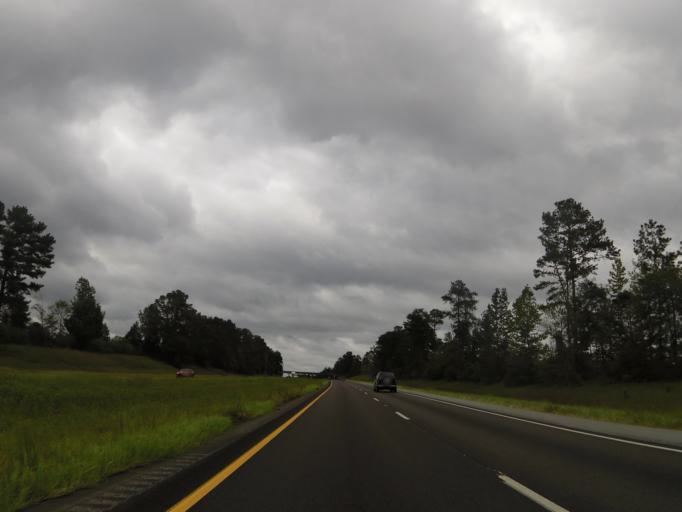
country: US
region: Alabama
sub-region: Conecuh County
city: Evergreen
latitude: 31.3531
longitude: -87.0776
